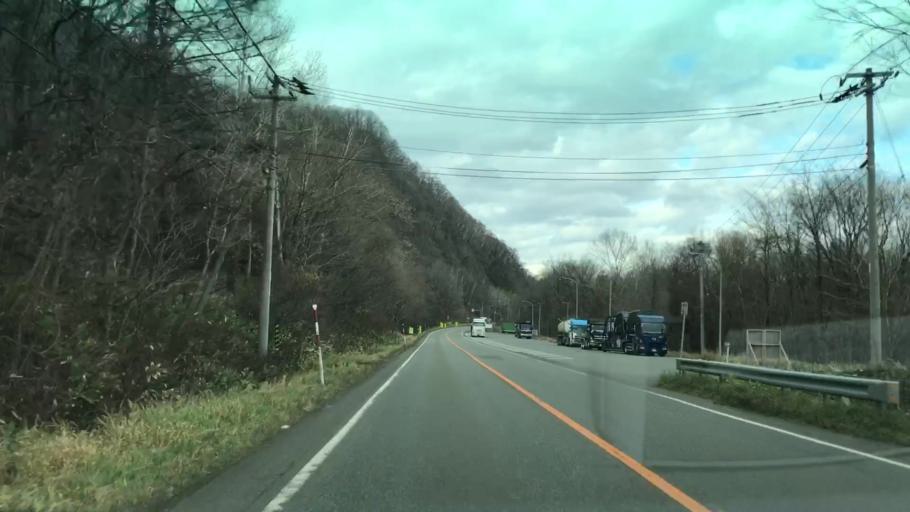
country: JP
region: Hokkaido
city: Shizunai-furukawacho
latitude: 42.8366
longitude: 142.4156
